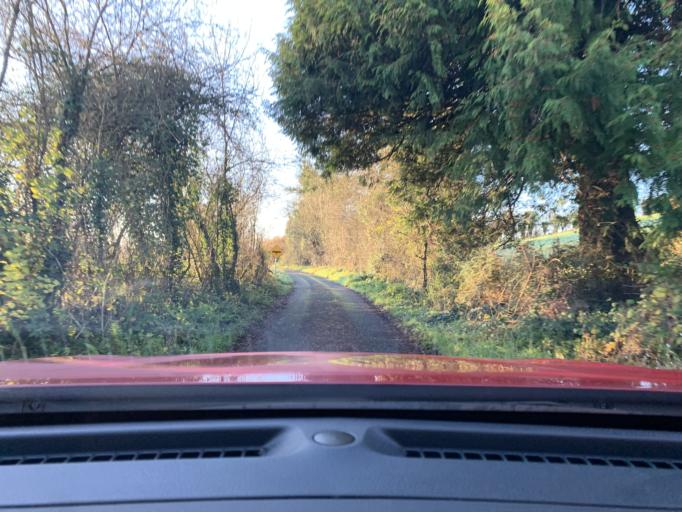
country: IE
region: Connaught
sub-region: Sligo
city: Ballymote
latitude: 54.0597
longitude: -8.5179
